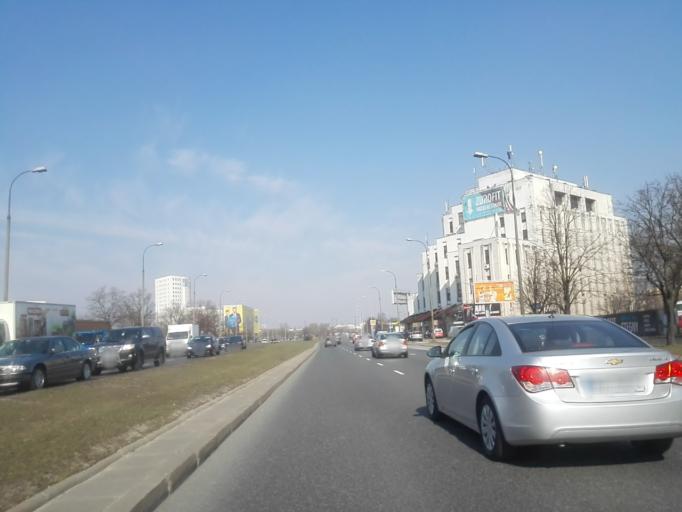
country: PL
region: Masovian Voivodeship
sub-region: Warszawa
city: Mokotow
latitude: 52.1859
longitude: 21.0460
